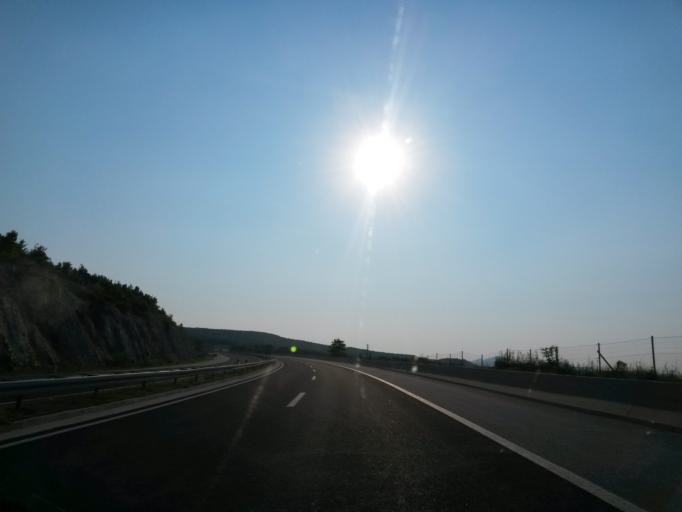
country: HR
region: Splitsko-Dalmatinska
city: Greda
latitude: 43.5823
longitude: 16.6579
